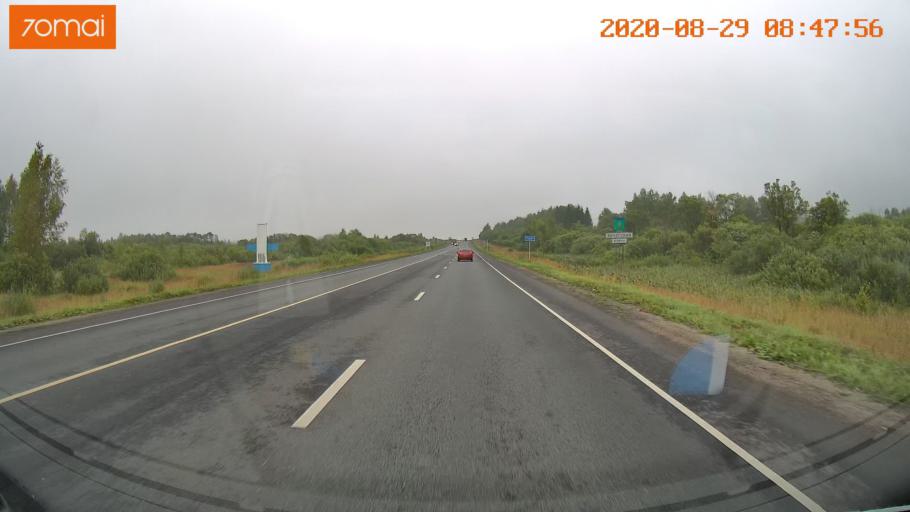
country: RU
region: Ivanovo
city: Vichuga
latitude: 57.1556
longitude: 41.8408
